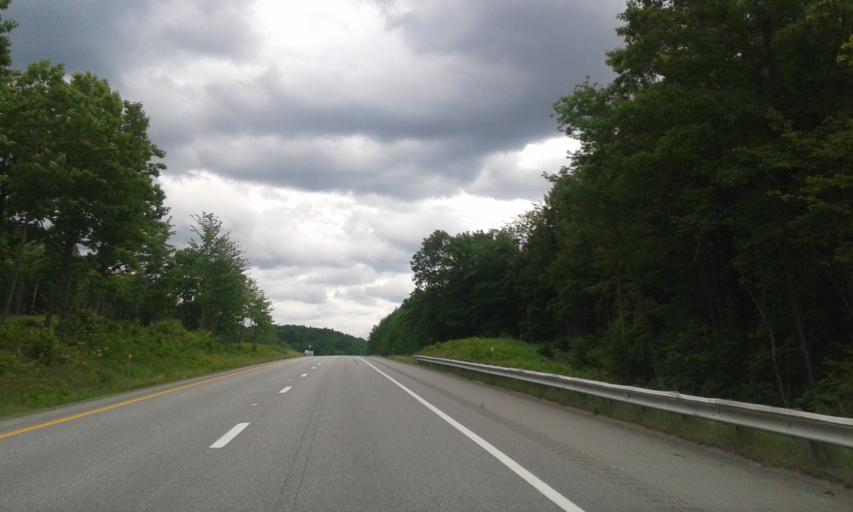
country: US
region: New Hampshire
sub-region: Belknap County
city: Tilton
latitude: 43.4448
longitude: -71.5746
